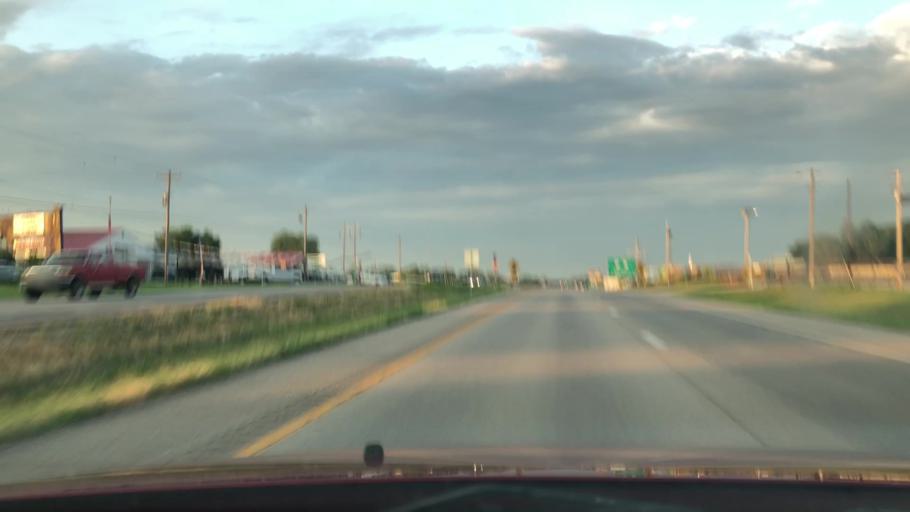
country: US
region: Missouri
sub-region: Greene County
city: Battlefield
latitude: 37.1583
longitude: -93.4049
